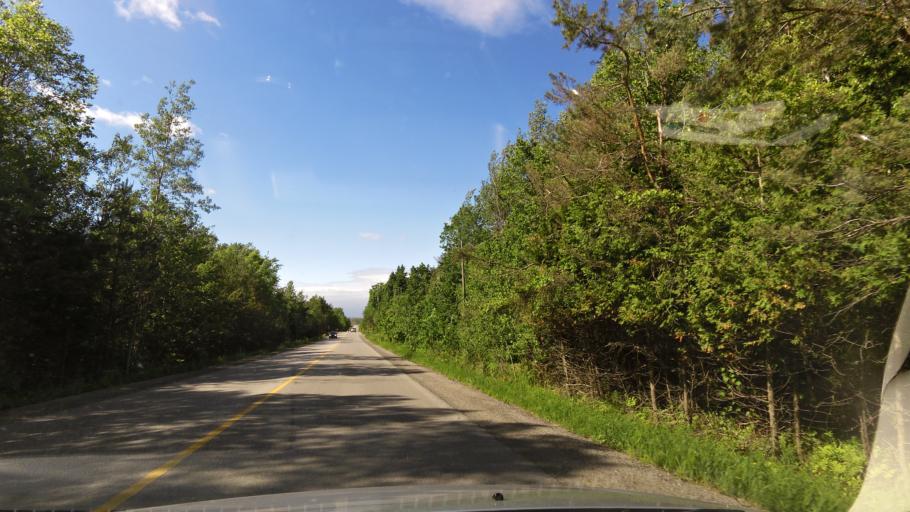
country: CA
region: Ontario
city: Bradford West Gwillimbury
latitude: 44.1959
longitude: -79.6241
